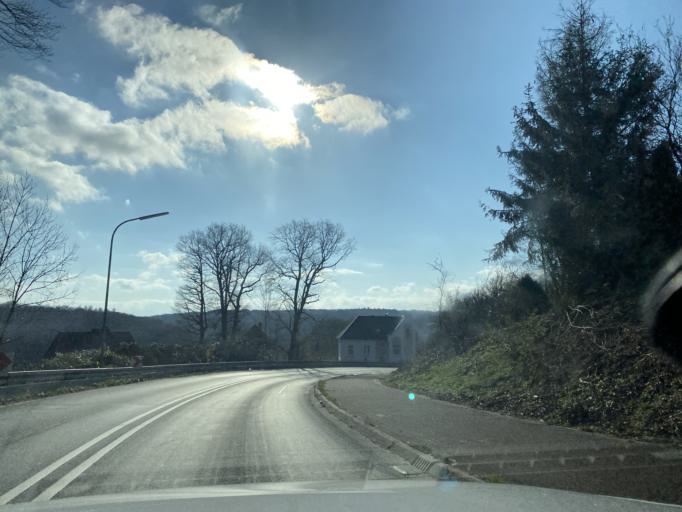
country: DE
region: North Rhine-Westphalia
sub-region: Regierungsbezirk Koln
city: Odenthal
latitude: 51.0576
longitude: 7.1271
